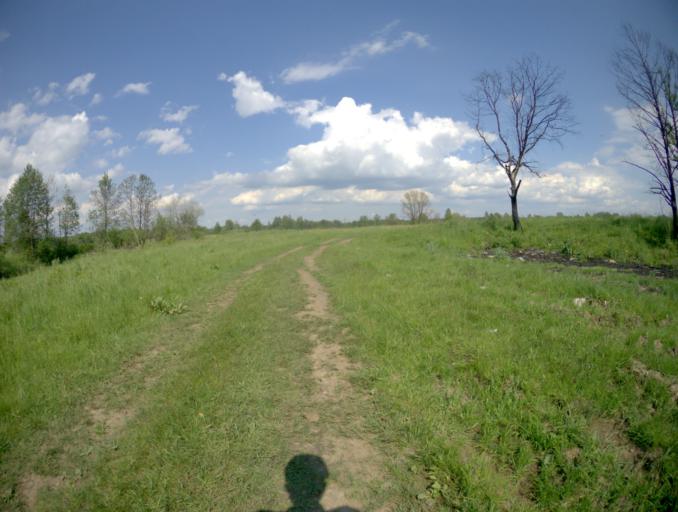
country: RU
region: Vladimir
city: Raduzhnyy
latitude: 56.0427
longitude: 40.3140
